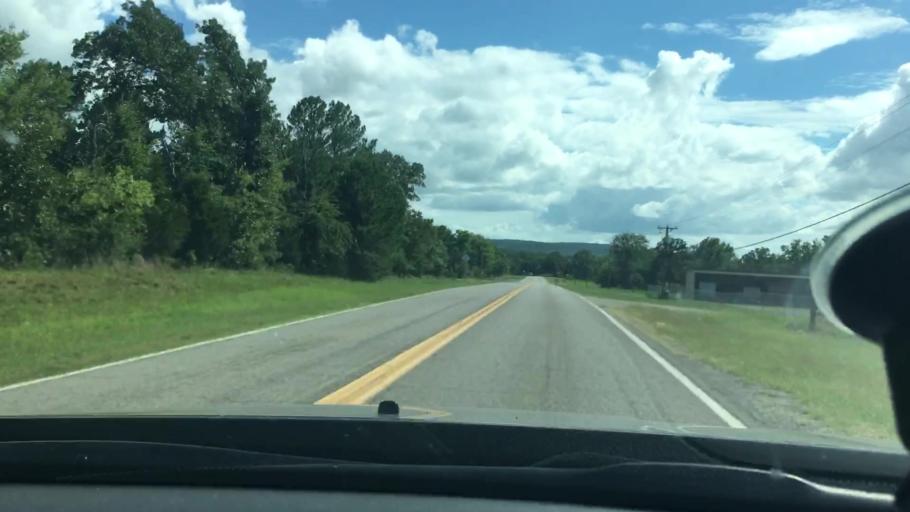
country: US
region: Oklahoma
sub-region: Cherokee County
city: Park Hill
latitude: 35.6989
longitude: -94.9144
